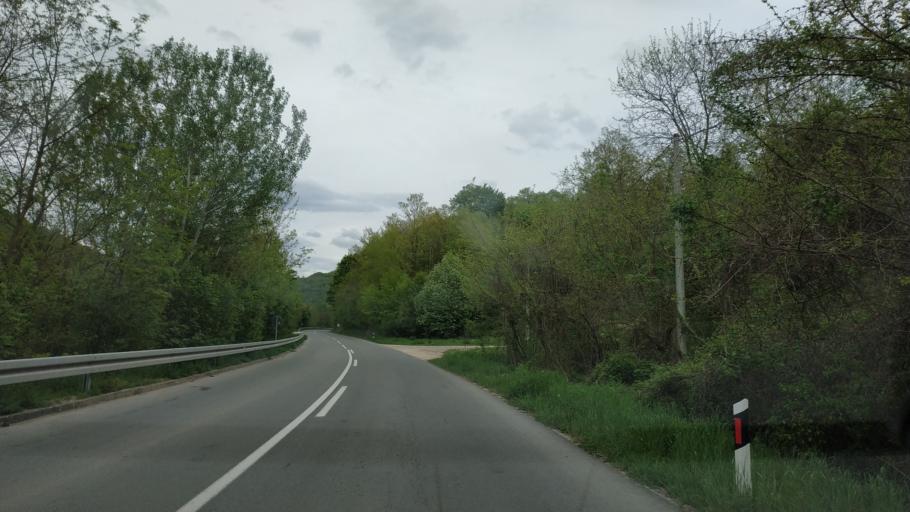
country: RS
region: Central Serbia
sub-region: Nisavski Okrug
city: Aleksinac
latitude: 43.6512
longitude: 21.7262
